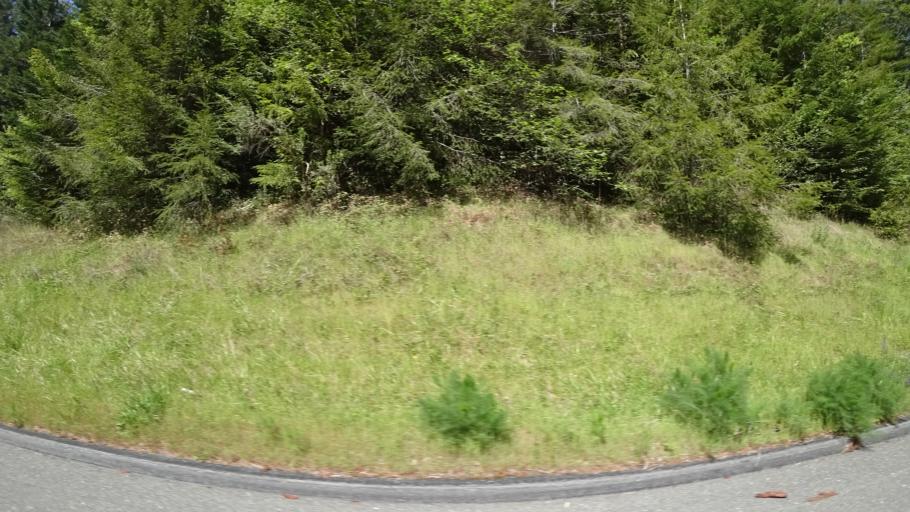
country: US
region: California
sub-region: Humboldt County
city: Westhaven-Moonstone
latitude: 41.3621
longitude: -123.9899
